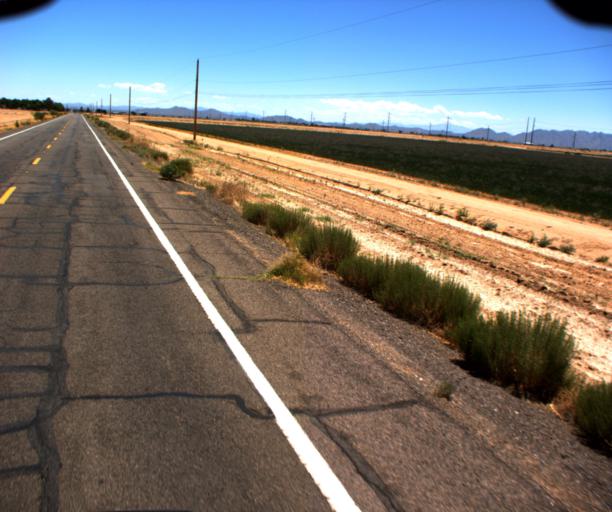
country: US
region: Arizona
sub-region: Pinal County
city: Coolidge
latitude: 32.8795
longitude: -111.5569
